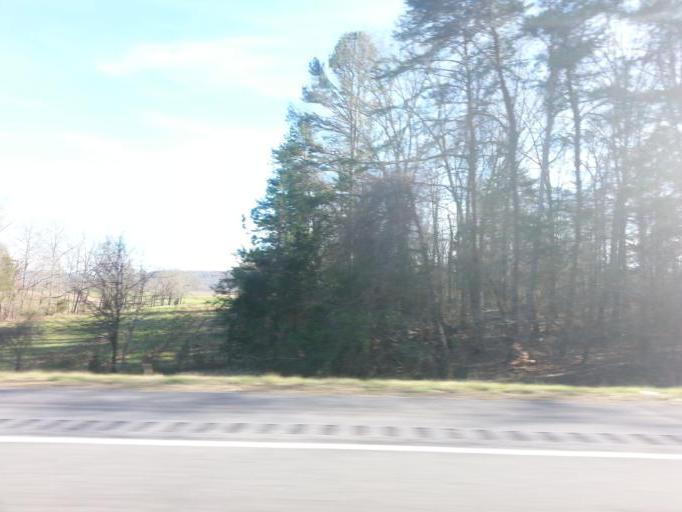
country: US
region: Tennessee
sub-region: Warren County
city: McMinnville
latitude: 35.7215
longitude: -85.6802
